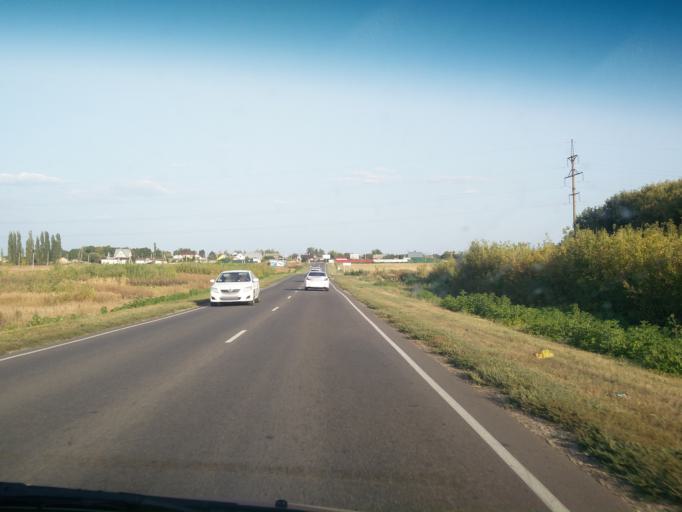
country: RU
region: Voronezj
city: Ramon'
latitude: 51.9353
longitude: 39.3400
